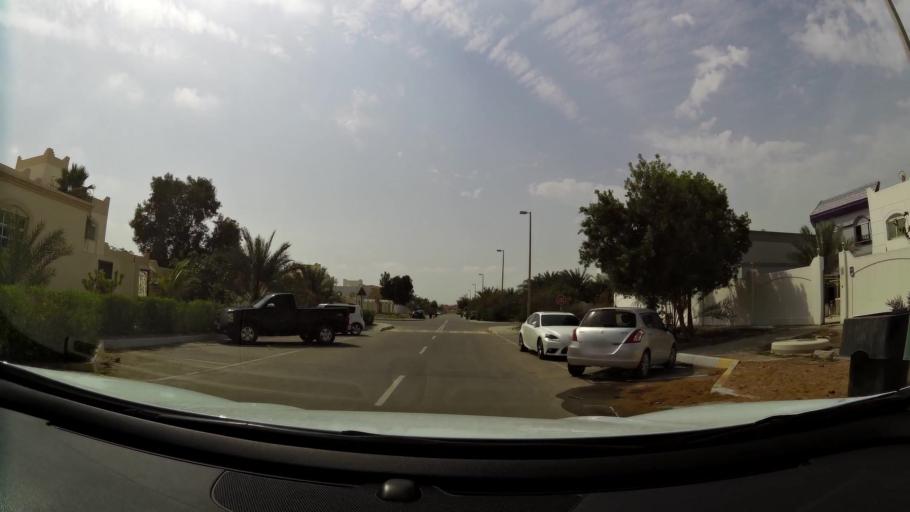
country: AE
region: Abu Dhabi
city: Abu Dhabi
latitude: 24.5458
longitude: 54.6335
